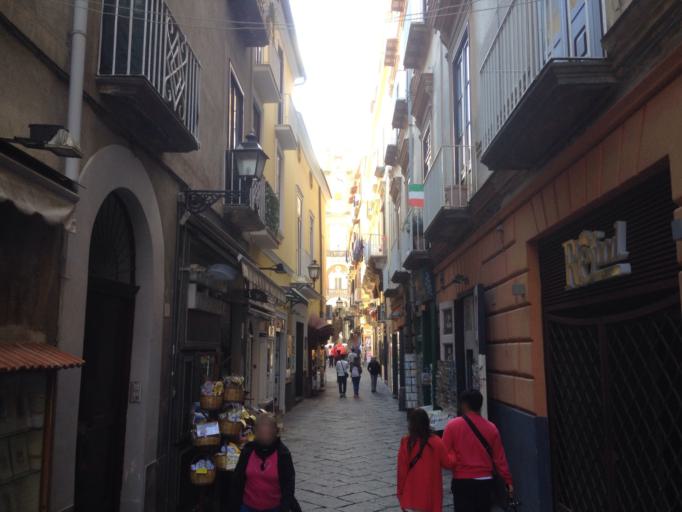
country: IT
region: Campania
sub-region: Provincia di Napoli
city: Sorrento
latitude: 40.6264
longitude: 14.3730
